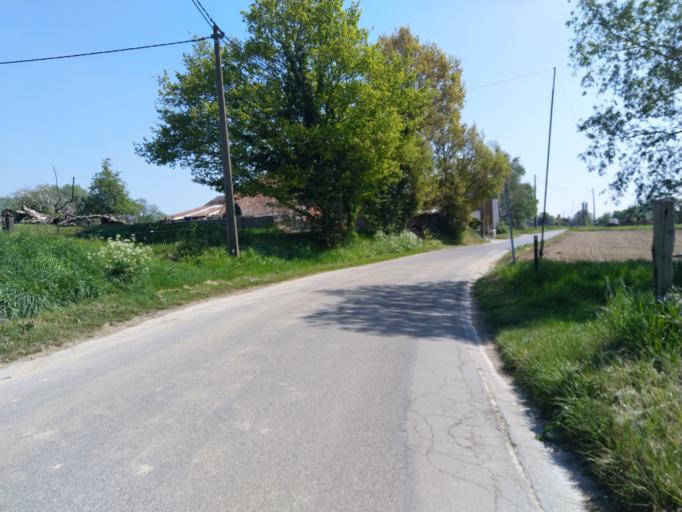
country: BE
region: Wallonia
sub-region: Province du Brabant Wallon
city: Rebecq-Rognon
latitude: 50.6307
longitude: 4.0810
